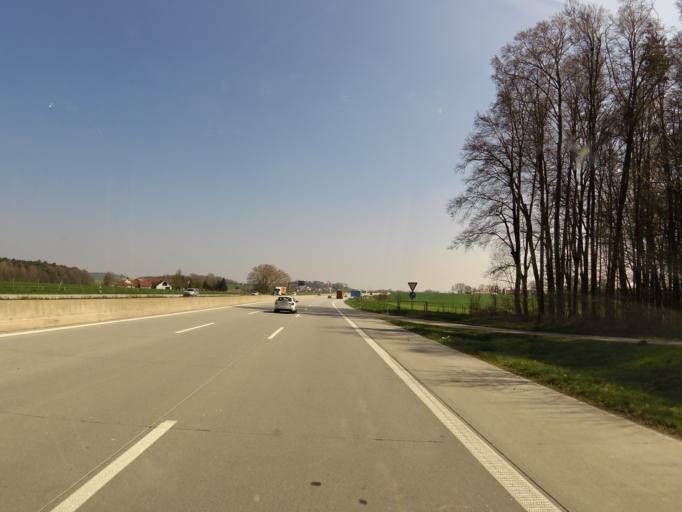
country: DE
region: Bavaria
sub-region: Upper Bavaria
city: Sulzemoos
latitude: 48.2767
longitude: 11.2785
